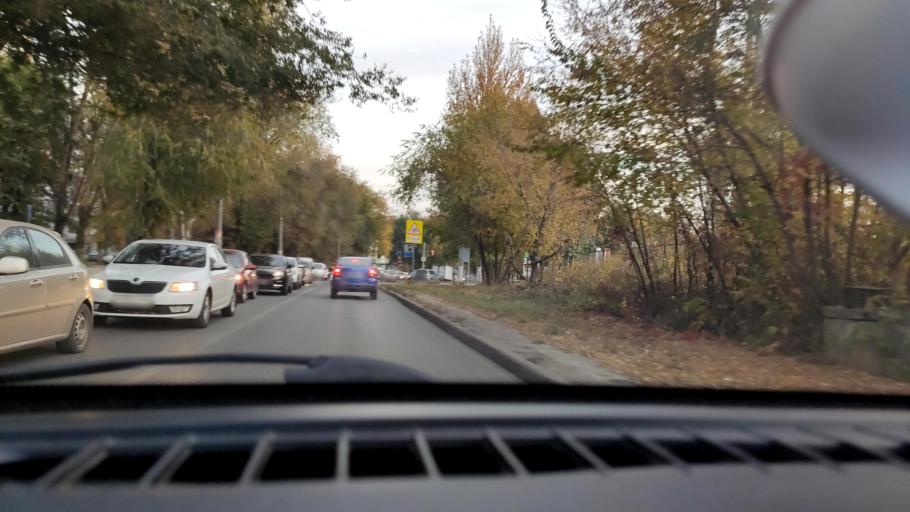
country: RU
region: Samara
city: Samara
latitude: 53.2431
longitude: 50.2549
